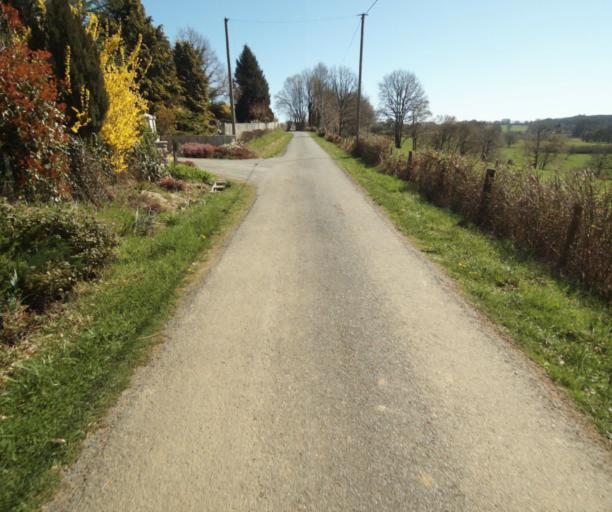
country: FR
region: Limousin
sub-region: Departement de la Correze
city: Uzerche
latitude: 45.4045
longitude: 1.6219
